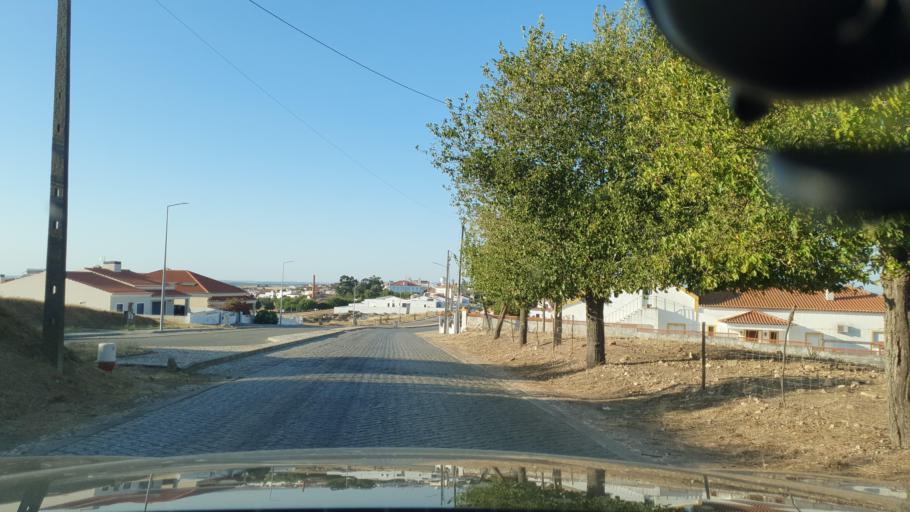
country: PT
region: Portalegre
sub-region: Fronteira
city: Fronteira
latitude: 38.9444
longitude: -7.6772
